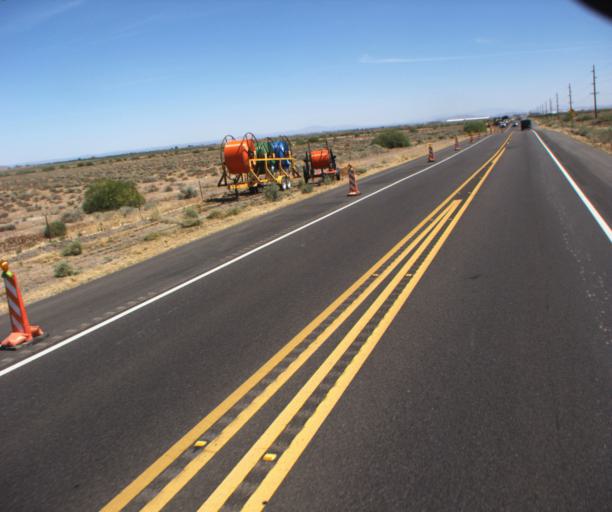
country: US
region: Arizona
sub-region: Pinal County
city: Blackwater
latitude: 33.0193
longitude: -111.6332
